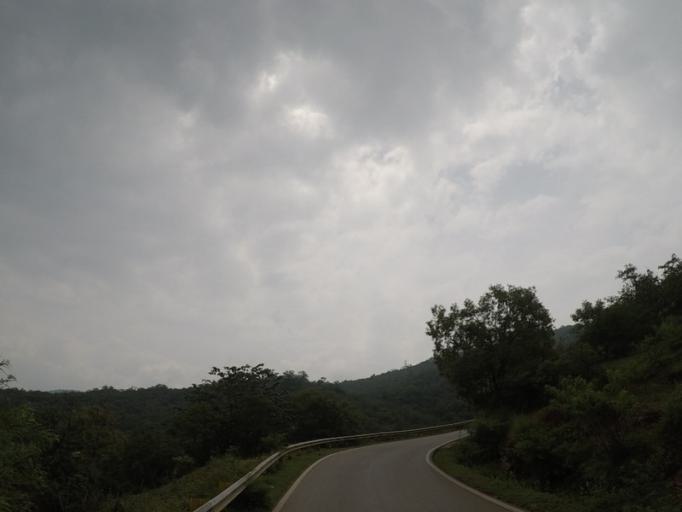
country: IN
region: Karnataka
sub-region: Chikmagalur
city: Birur
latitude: 13.5511
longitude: 75.8235
